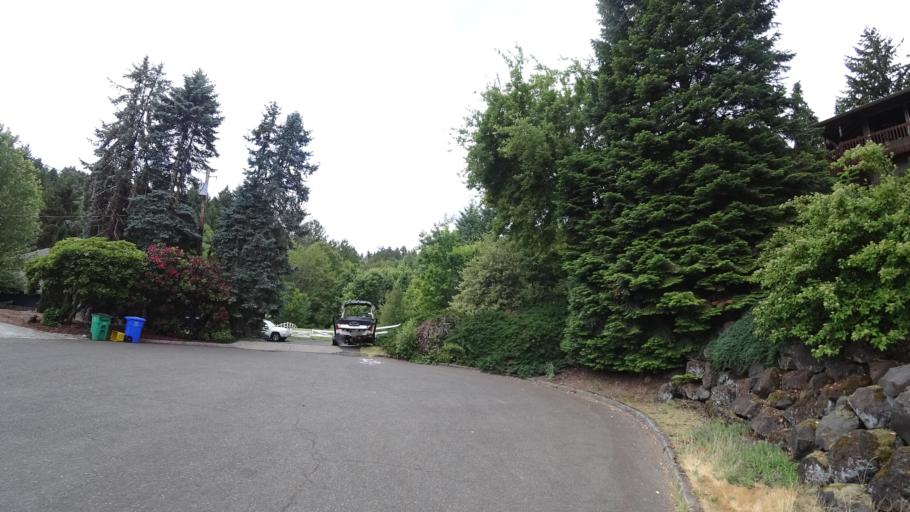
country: US
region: Oregon
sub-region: Clackamas County
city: Lake Oswego
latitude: 45.4560
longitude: -122.6970
